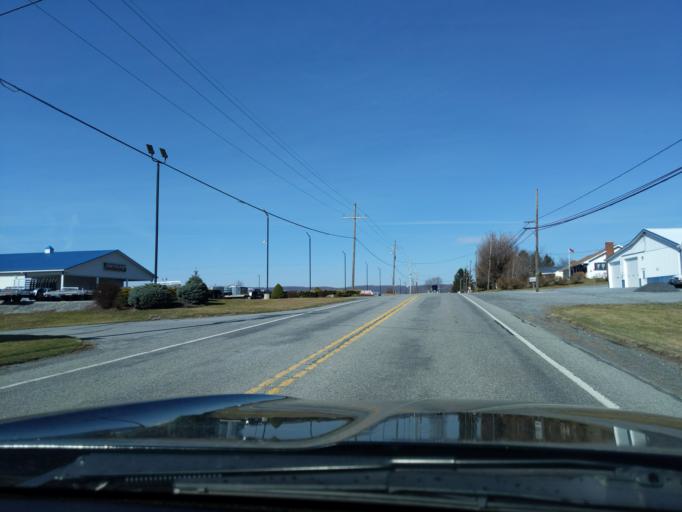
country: US
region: Pennsylvania
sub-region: Blair County
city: Martinsburg
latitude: 40.3220
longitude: -78.3471
